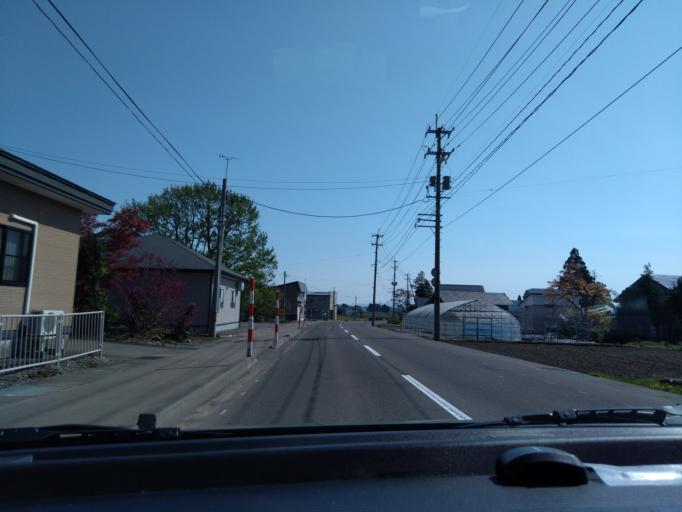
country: JP
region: Akita
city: Omagari
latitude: 39.4542
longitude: 140.5775
